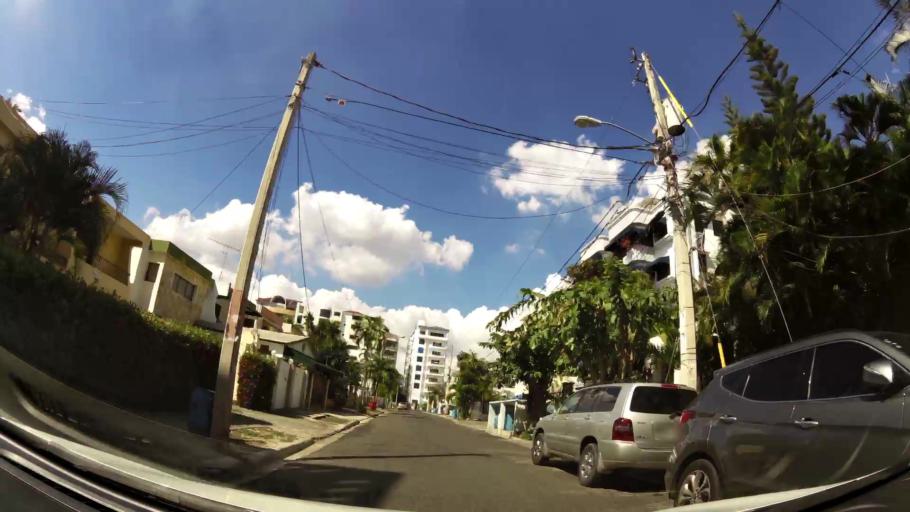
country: DO
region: Santiago
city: Santiago de los Caballeros
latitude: 19.4536
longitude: -70.6834
